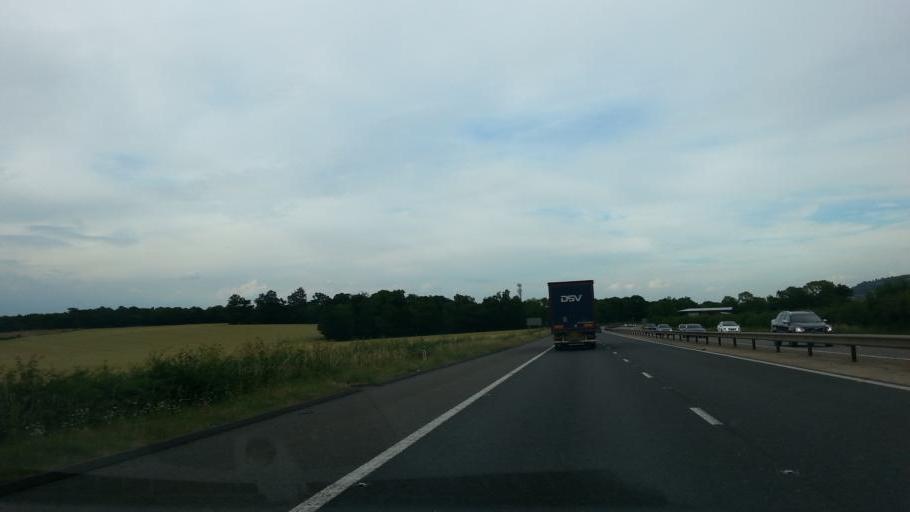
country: GB
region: England
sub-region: Worcestershire
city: Bredon
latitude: 52.0432
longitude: -2.1472
